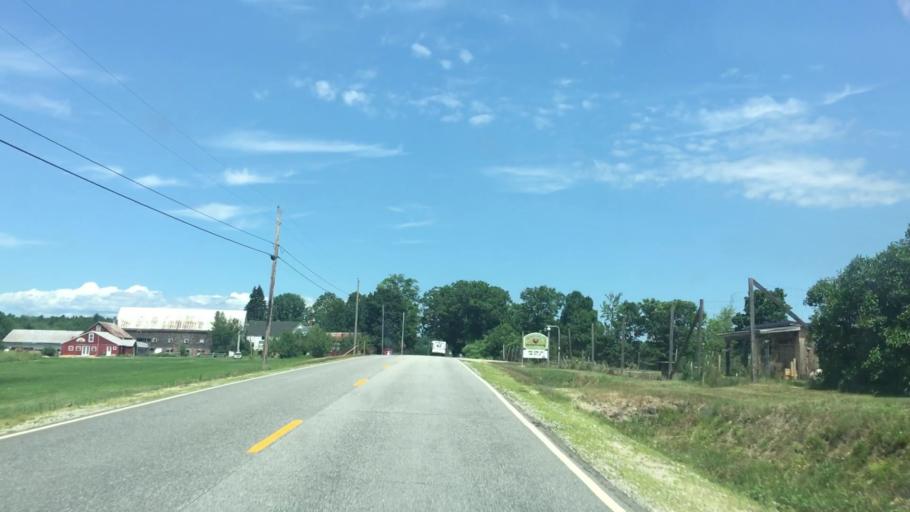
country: US
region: Maine
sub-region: Androscoggin County
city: Livermore
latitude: 44.3752
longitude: -70.2059
